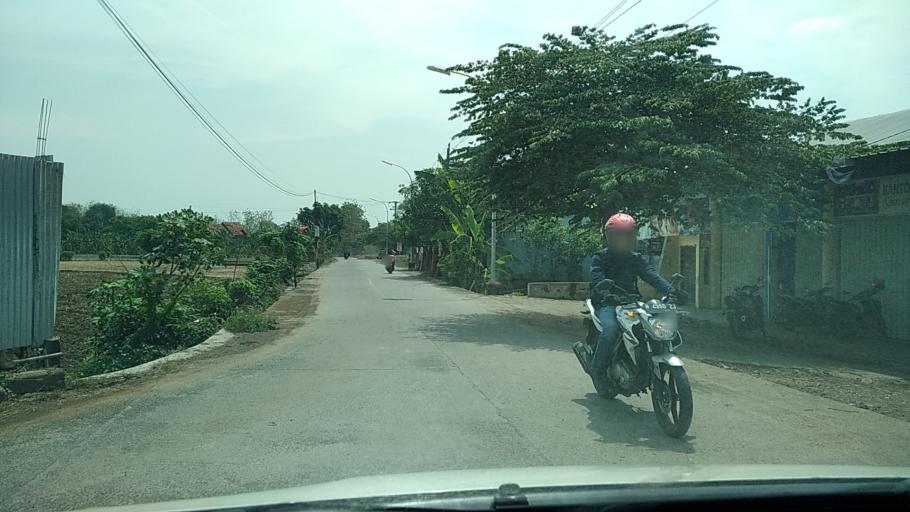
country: ID
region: Central Java
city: Mranggen
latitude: -7.0598
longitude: 110.4759
